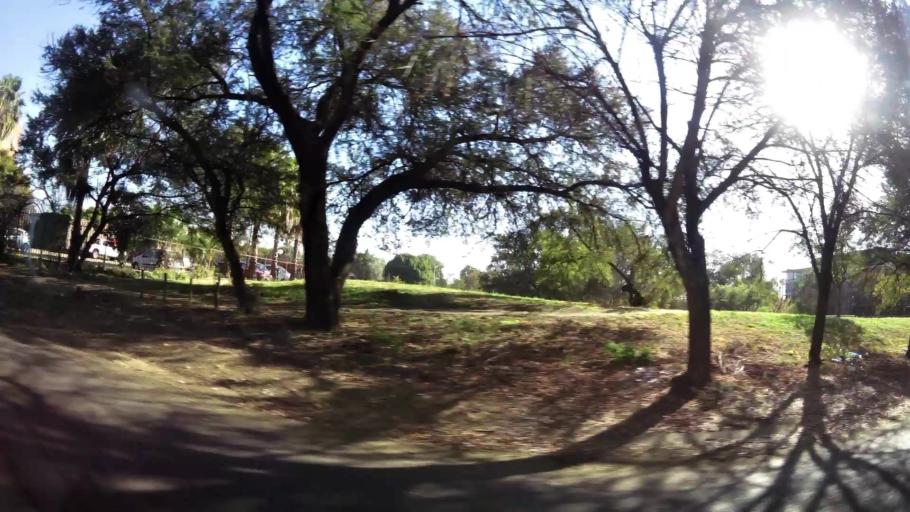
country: ZA
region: Gauteng
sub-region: City of Tshwane Metropolitan Municipality
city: Pretoria
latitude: -25.7212
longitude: 28.2623
